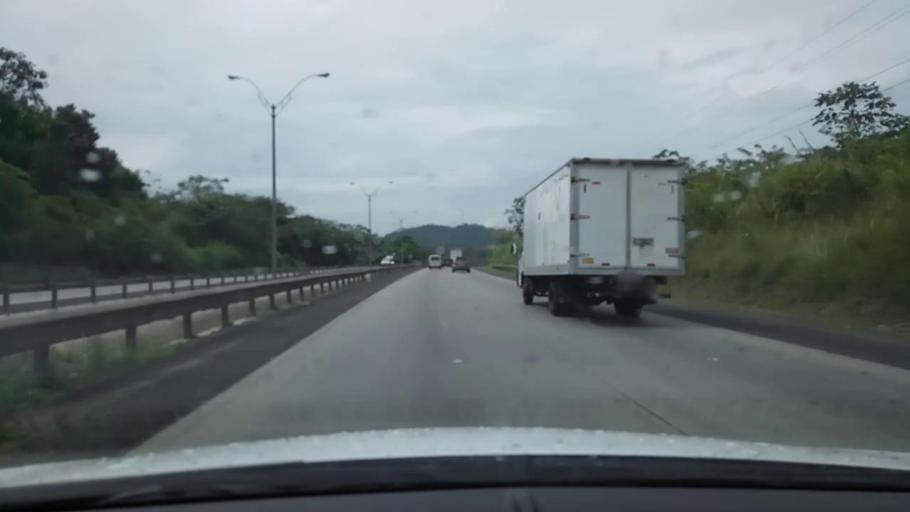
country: PA
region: Panama
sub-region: Distrito de Panama
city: Paraiso
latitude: 9.0279
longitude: -79.5915
